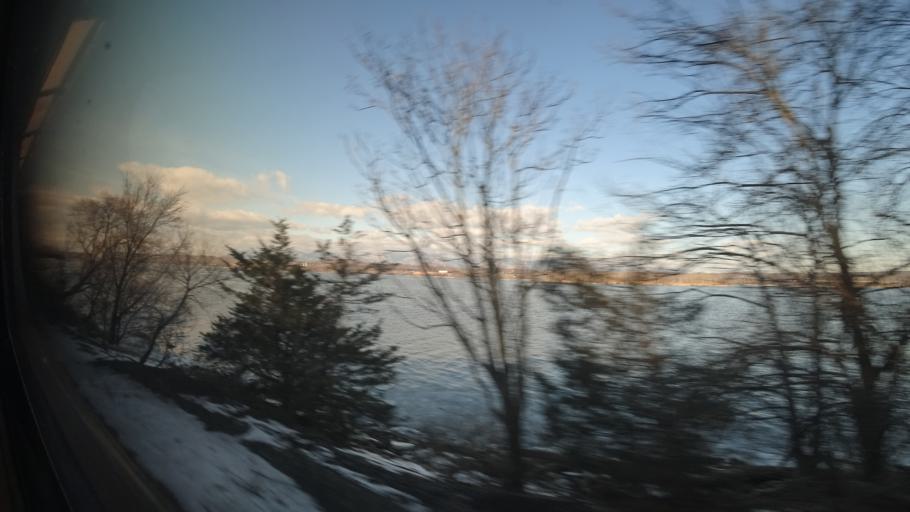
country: US
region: New York
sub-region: Greene County
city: Catskill
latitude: 42.1637
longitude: -73.8809
